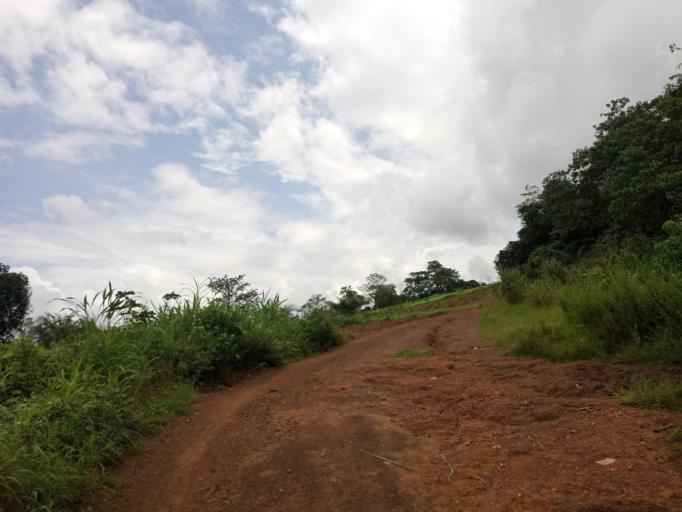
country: SL
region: Northern Province
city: Kamakwie
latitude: 9.4806
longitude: -12.2449
